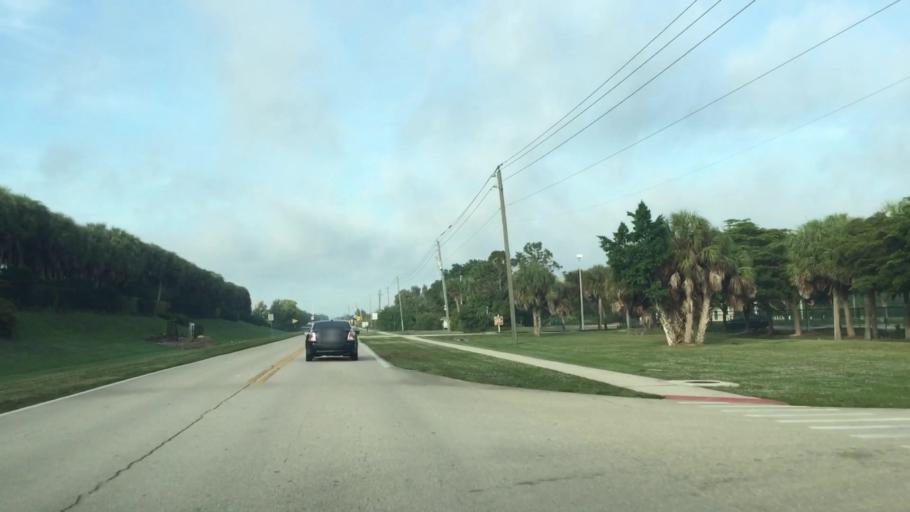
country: US
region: Florida
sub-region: Lee County
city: Estero
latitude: 26.4204
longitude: -81.8016
